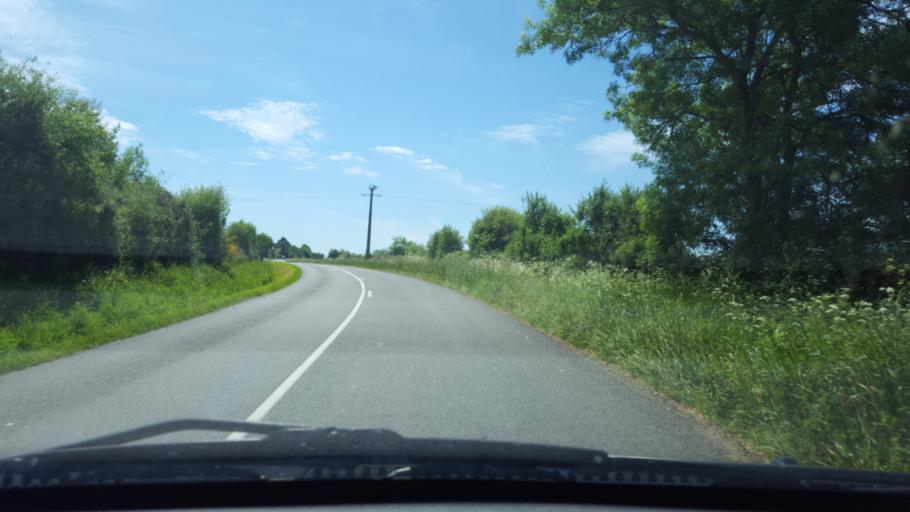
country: FR
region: Pays de la Loire
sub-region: Departement de la Loire-Atlantique
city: Saint-Philbert-de-Grand-Lieu
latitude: 46.9832
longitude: -1.6688
